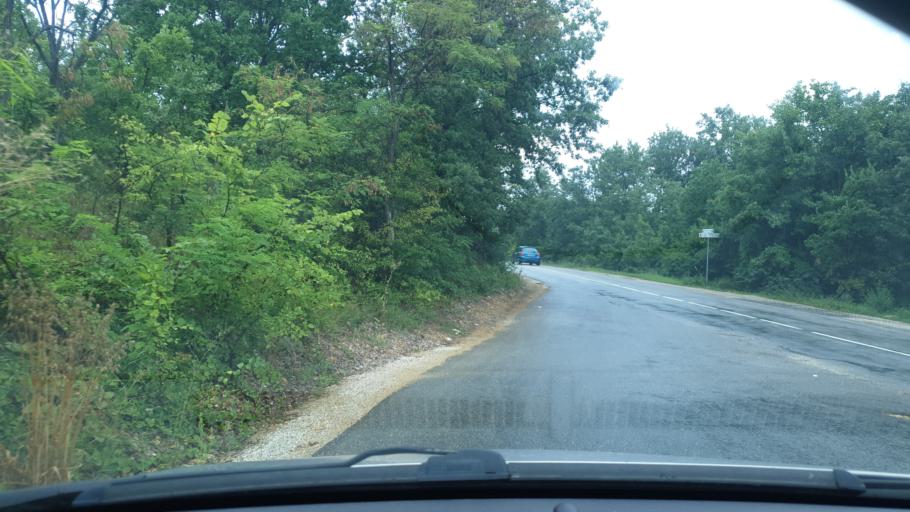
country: RS
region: Central Serbia
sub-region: Sumadijski Okrug
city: Kragujevac
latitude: 44.0517
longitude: 20.7828
